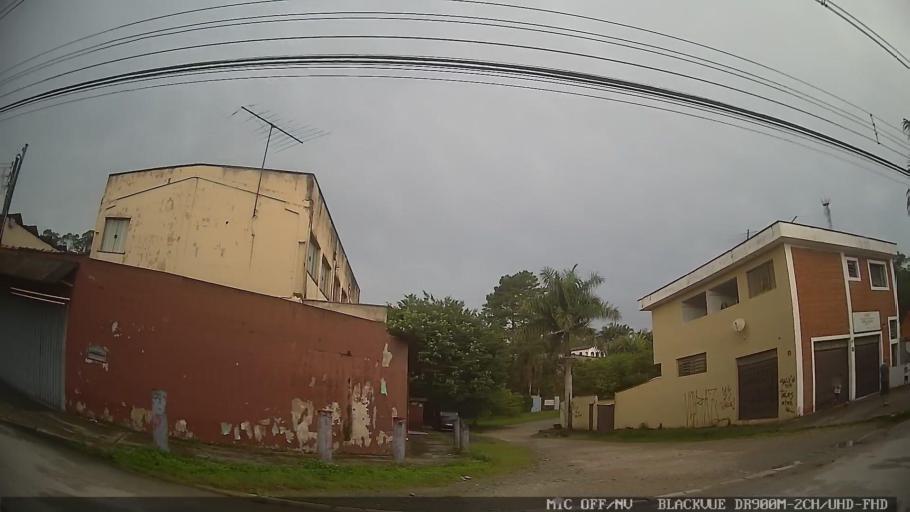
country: BR
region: Sao Paulo
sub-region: Ribeirao Pires
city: Ribeirao Pires
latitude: -23.6826
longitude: -46.3531
